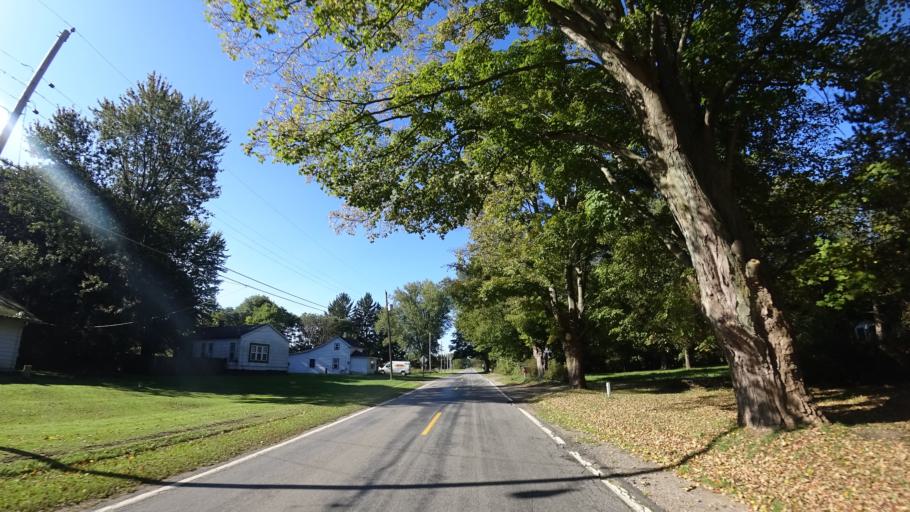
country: US
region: Michigan
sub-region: Berrien County
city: Benton Heights
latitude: 42.1725
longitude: -86.3897
